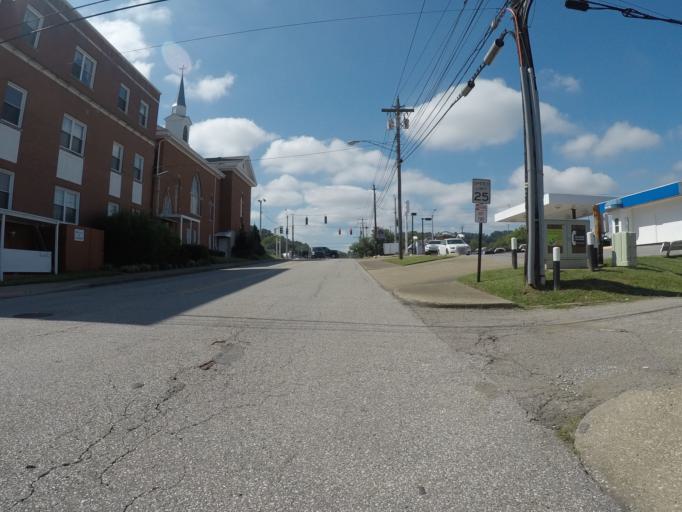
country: US
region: Kentucky
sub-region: Boyd County
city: Ashland
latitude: 38.4704
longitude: -82.6230
